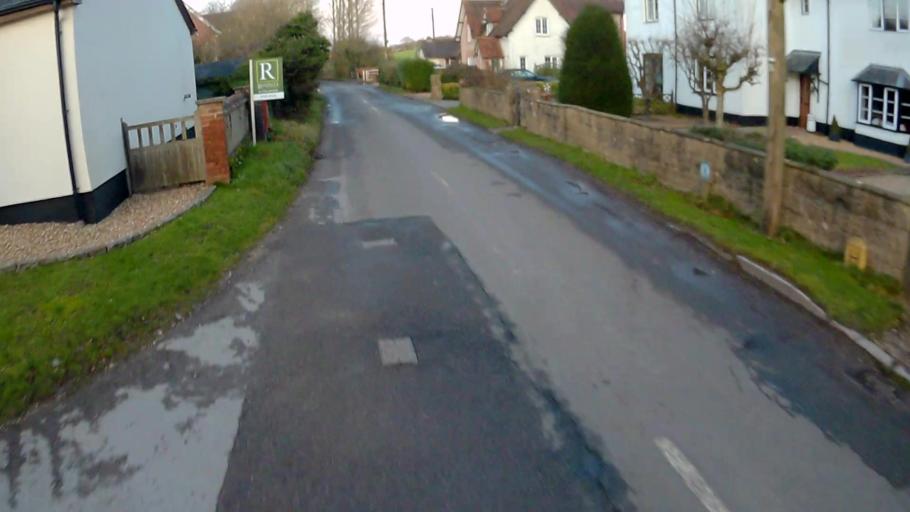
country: GB
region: England
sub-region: Hampshire
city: Overton
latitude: 51.2397
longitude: -1.2186
